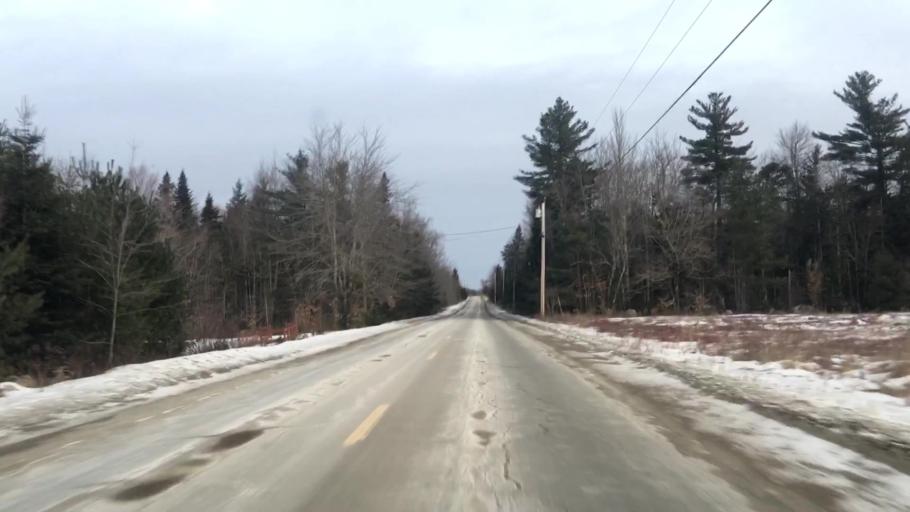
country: US
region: Maine
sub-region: Hancock County
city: Franklin
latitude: 44.7272
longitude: -68.3349
